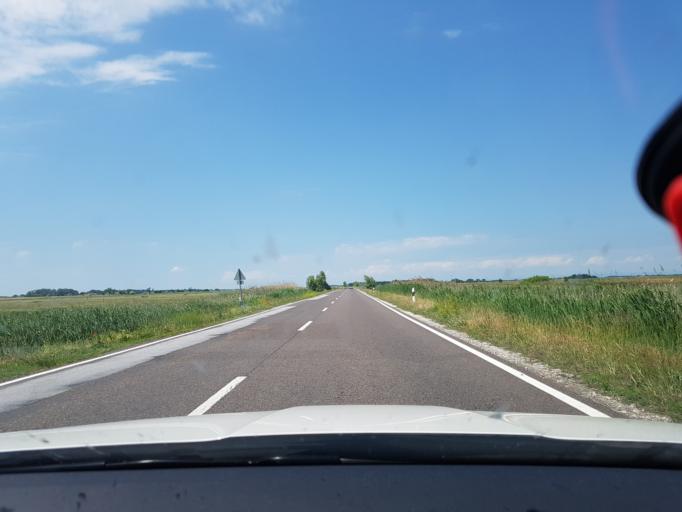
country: HU
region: Hajdu-Bihar
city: Egyek
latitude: 47.5521
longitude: 20.8789
